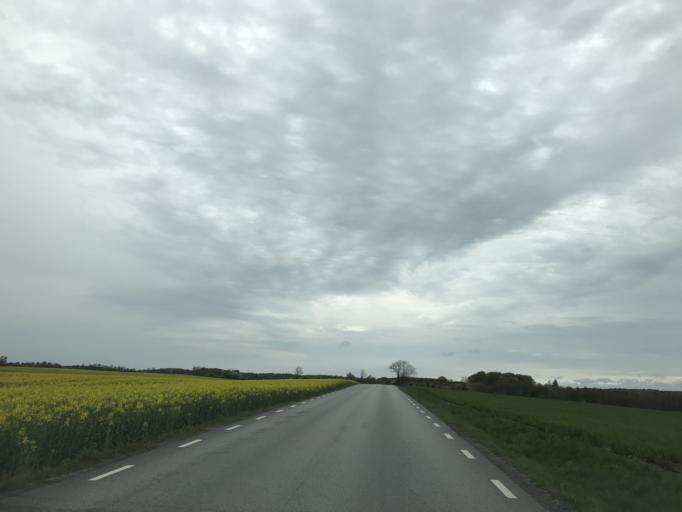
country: SE
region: Skane
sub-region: Trelleborgs Kommun
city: Anderslov
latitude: 55.4925
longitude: 13.3360
